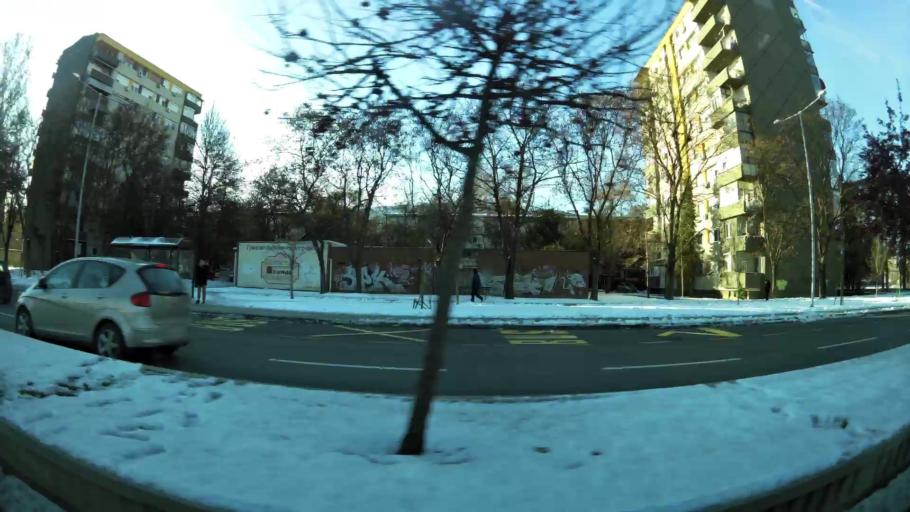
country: MK
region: Karpos
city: Skopje
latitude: 42.0074
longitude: 21.4000
